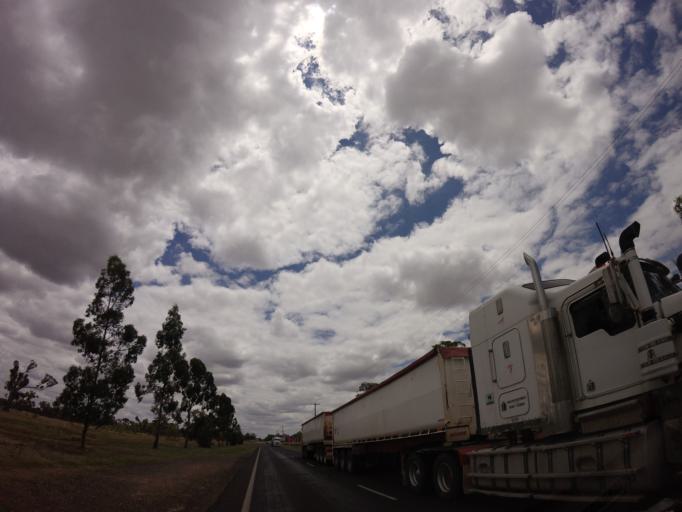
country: AU
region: Queensland
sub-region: Goondiwindi
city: Goondiwindi
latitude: -28.5136
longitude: 150.2892
